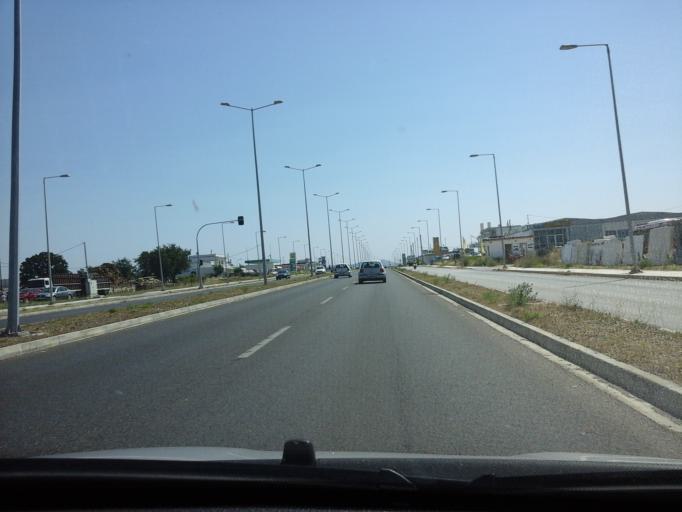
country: GR
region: East Macedonia and Thrace
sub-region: Nomos Evrou
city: Alexandroupoli
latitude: 40.8523
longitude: 25.9081
